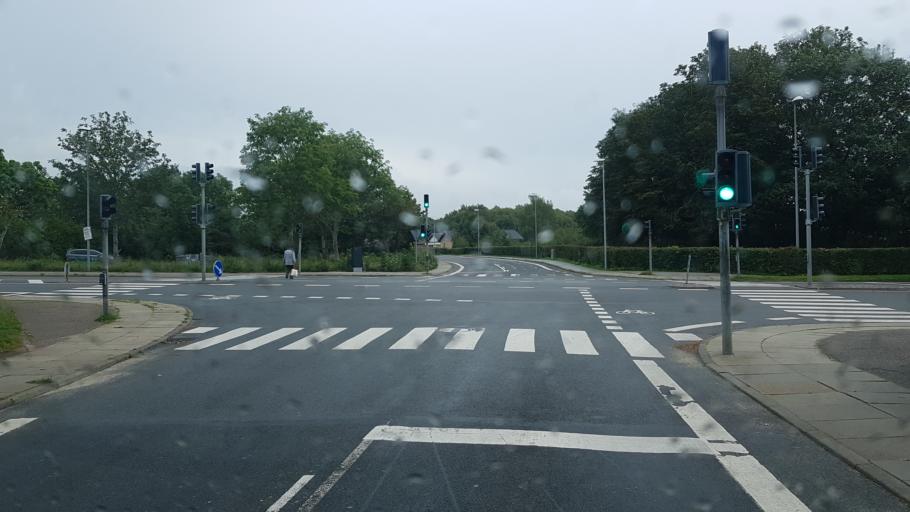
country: DK
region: Central Jutland
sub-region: Silkeborg Kommune
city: Silkeborg
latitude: 56.1830
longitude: 9.5560
